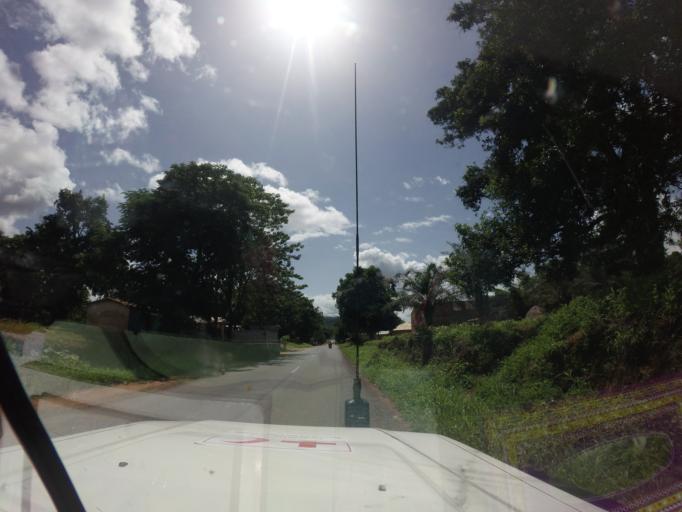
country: GN
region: Mamou
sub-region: Mamou Prefecture
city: Mamou
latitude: 10.1813
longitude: -11.8387
